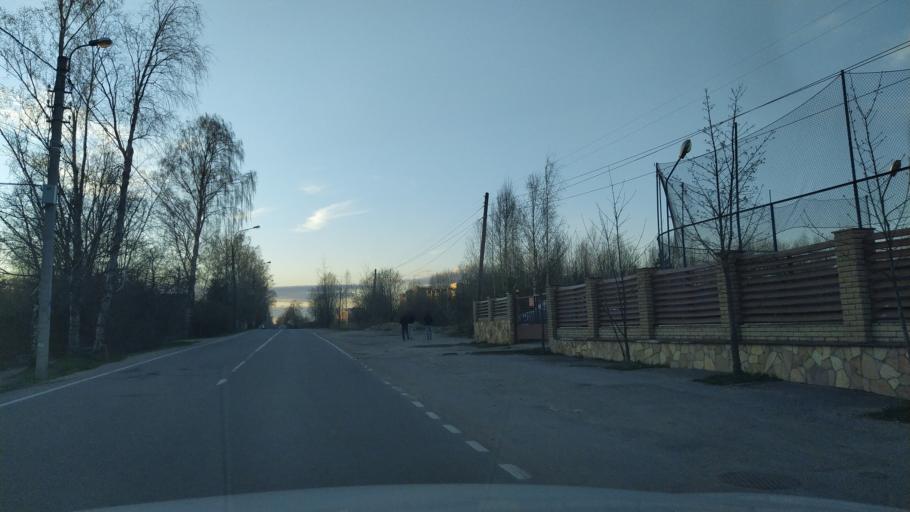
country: RU
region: St.-Petersburg
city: Pavlovsk
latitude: 59.6929
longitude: 30.4147
